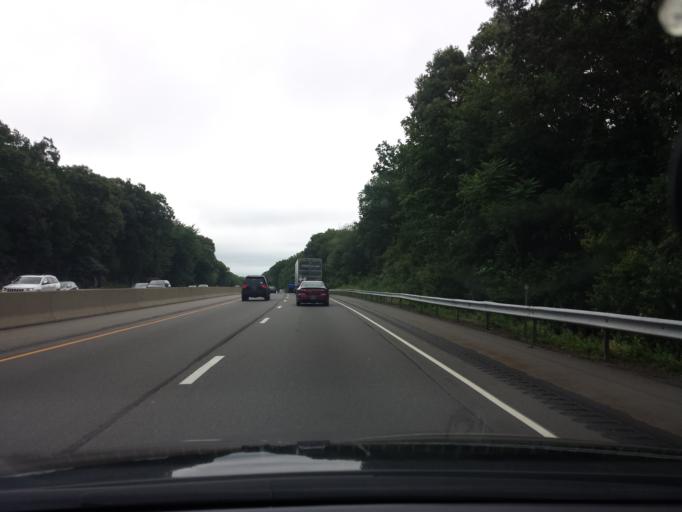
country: US
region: Connecticut
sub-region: Middlesex County
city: Clinton
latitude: 41.2881
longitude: -72.5566
